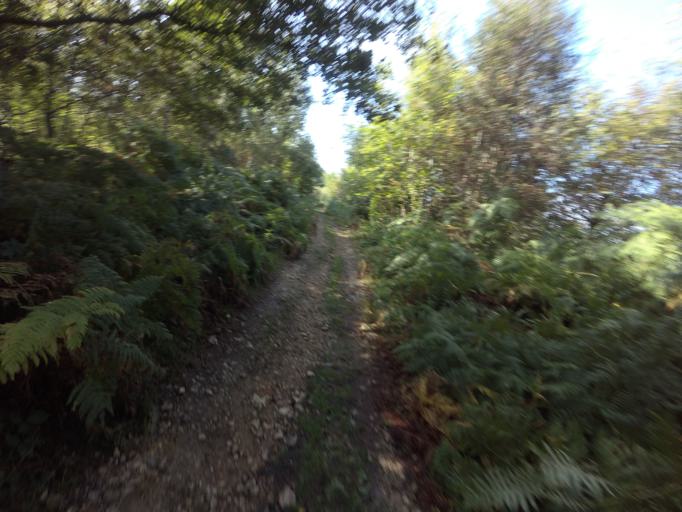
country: NL
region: Limburg
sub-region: Gemeente Vaals
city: Vaals
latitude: 50.7685
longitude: 5.9800
